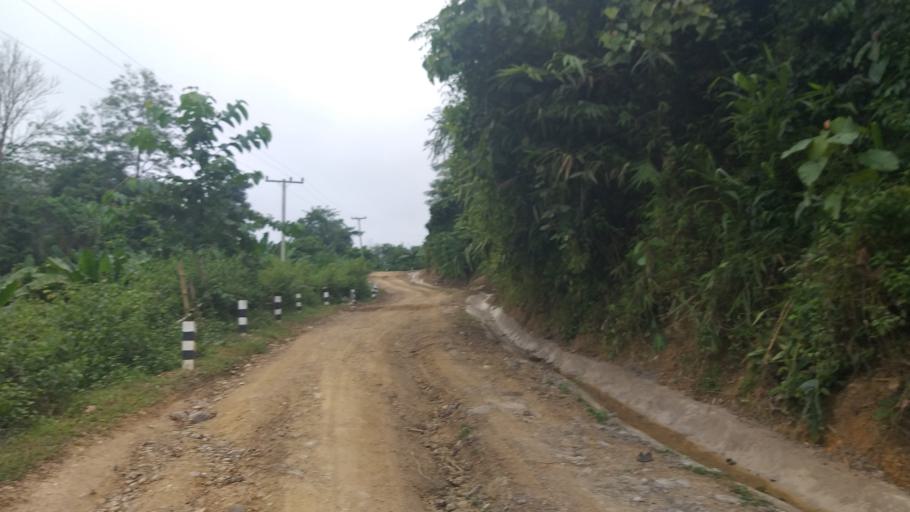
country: LA
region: Phongsali
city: Khoa
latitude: 21.2384
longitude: 102.6707
